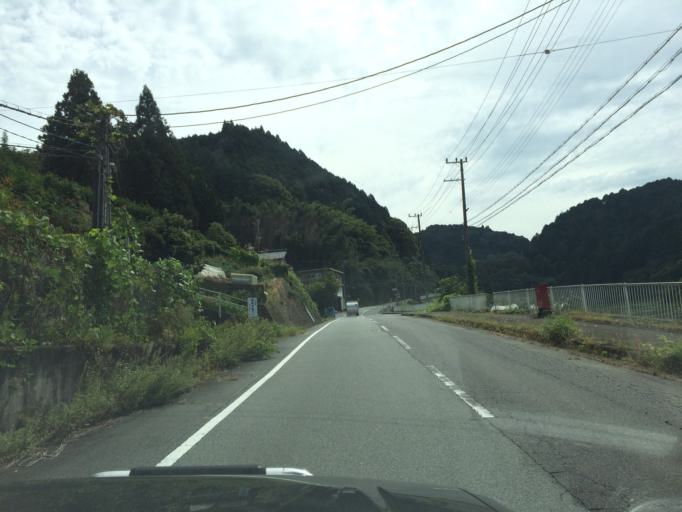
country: JP
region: Mie
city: Nabari
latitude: 34.6796
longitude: 135.9791
